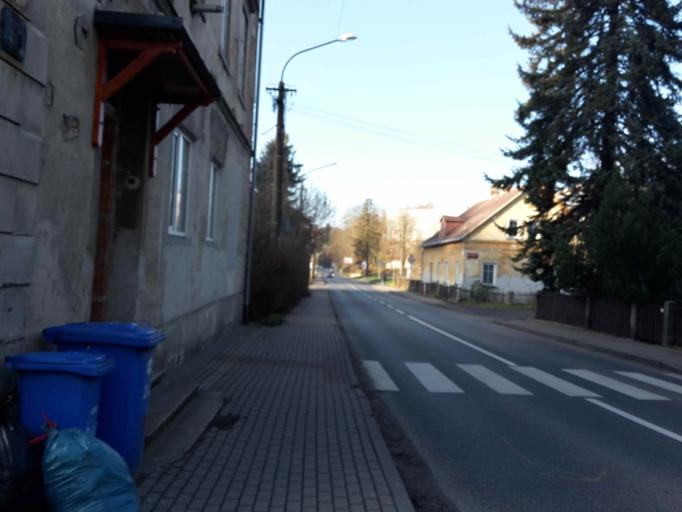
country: CZ
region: Liberecky
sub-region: Okres Liberec
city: Liberec
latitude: 50.7674
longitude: 15.0886
